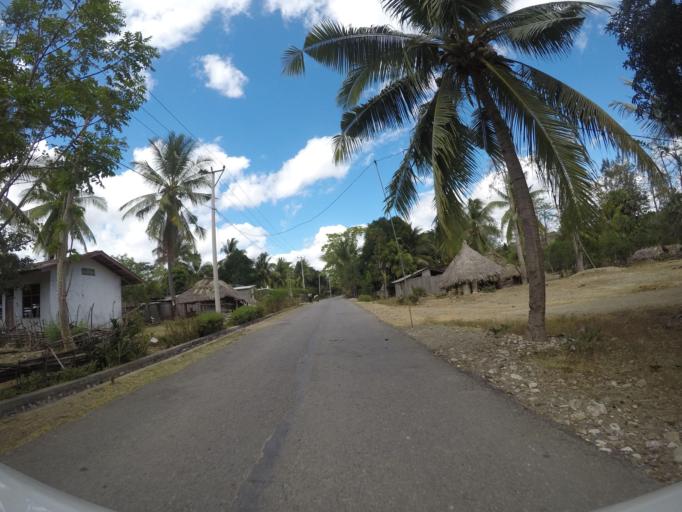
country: TL
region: Lautem
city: Lospalos
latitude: -8.4491
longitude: 126.8237
